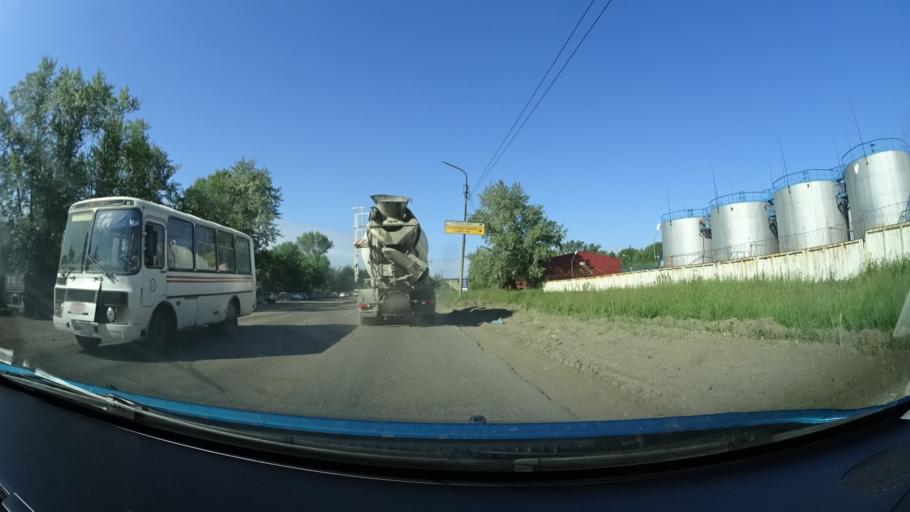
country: RU
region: Bashkortostan
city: Ufa
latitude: 54.8570
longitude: 56.1005
